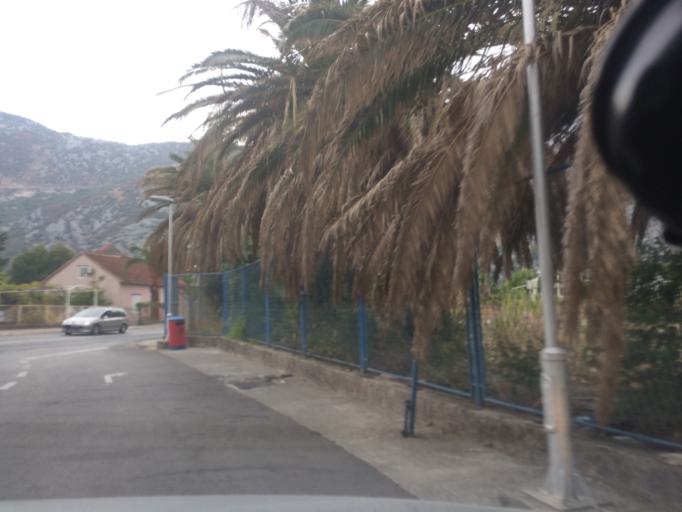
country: ME
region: Kotor
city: Risan
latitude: 42.5108
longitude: 18.6963
